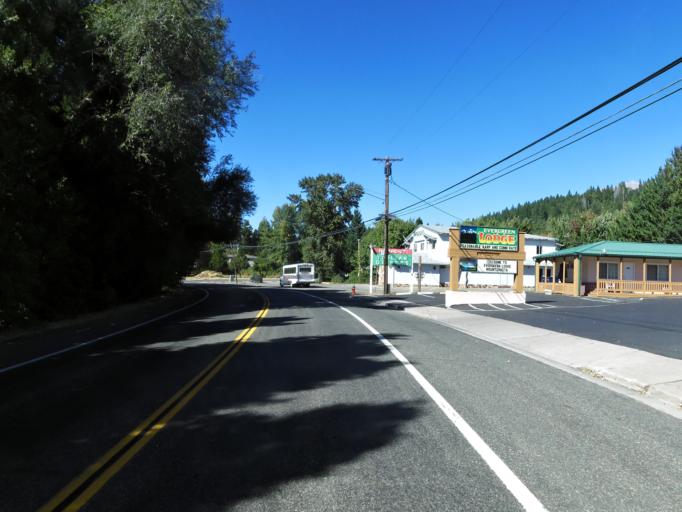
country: US
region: California
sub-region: Siskiyou County
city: Mount Shasta
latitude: 41.3013
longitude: -122.3062
